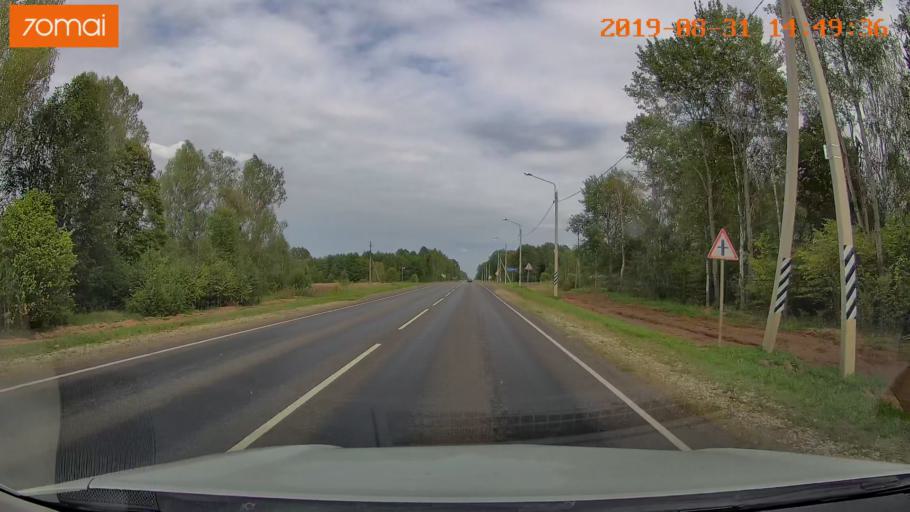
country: RU
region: Kaluga
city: Spas-Demensk
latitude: 54.2552
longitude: 33.7688
